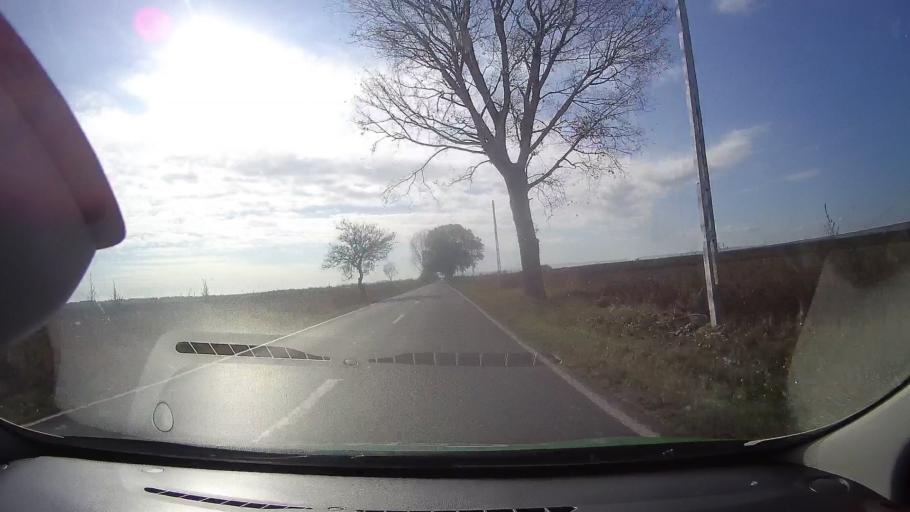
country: RO
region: Tulcea
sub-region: Comuna Valea Nucarilor
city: Agighiol
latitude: 44.9920
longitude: 28.8857
